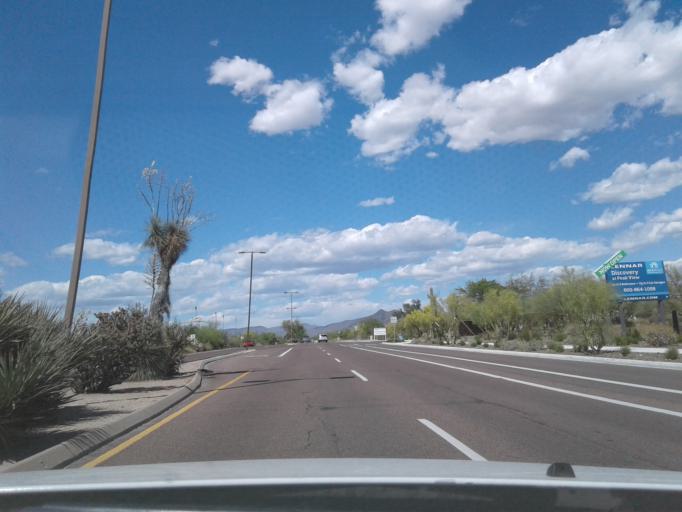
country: US
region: Arizona
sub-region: Maricopa County
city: Cave Creek
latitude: 33.7474
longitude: -111.9957
